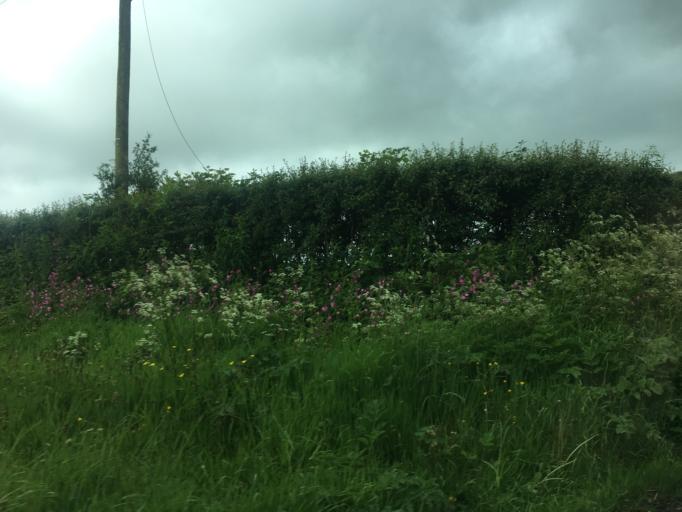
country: GB
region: Wales
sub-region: County of Ceredigion
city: Lampeter
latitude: 52.0773
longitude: -4.0394
